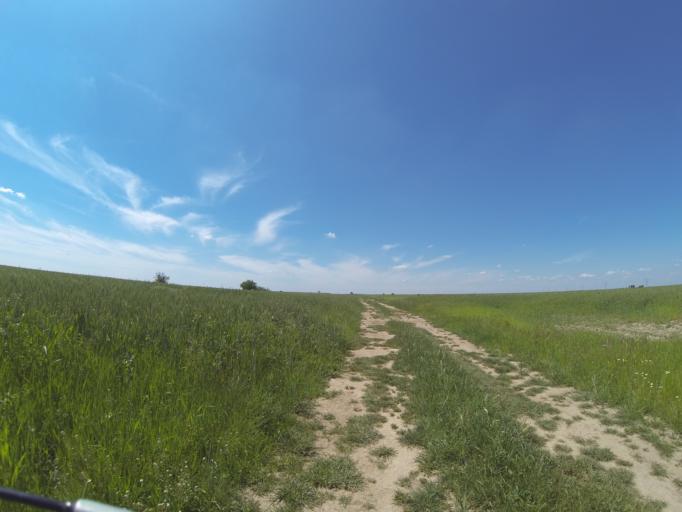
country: RO
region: Dolj
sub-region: Comuna Leu
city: Leu
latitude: 44.2120
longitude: 24.0302
